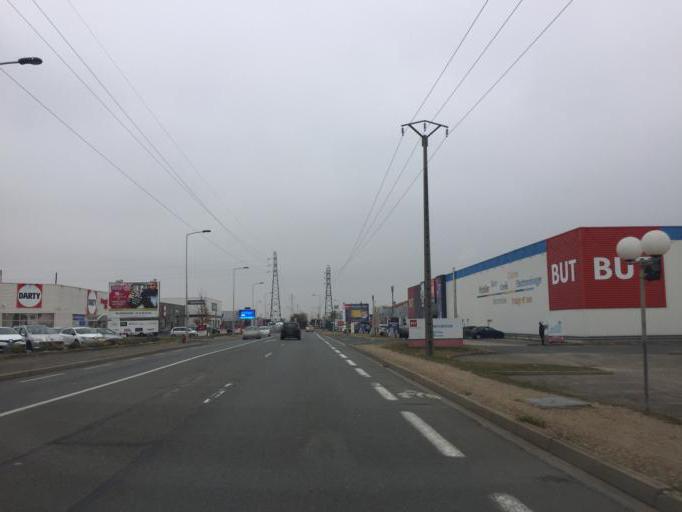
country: FR
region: Rhone-Alpes
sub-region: Departement de l'Ain
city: Jassans-Riottier
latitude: 45.9872
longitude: 4.7437
